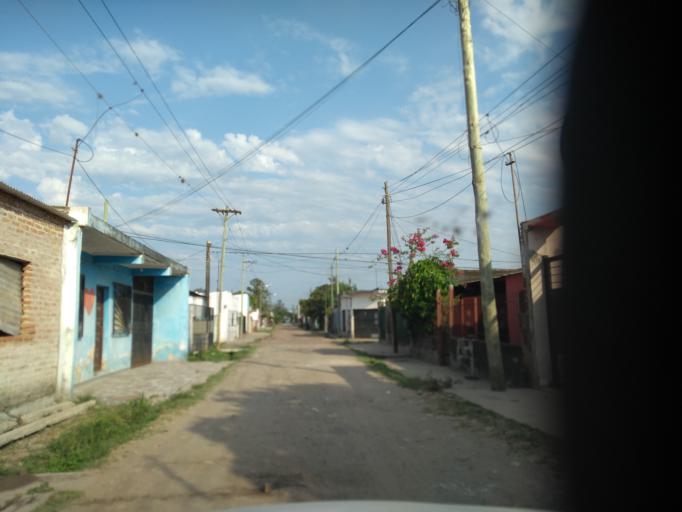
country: AR
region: Chaco
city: Resistencia
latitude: -27.4716
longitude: -58.9746
